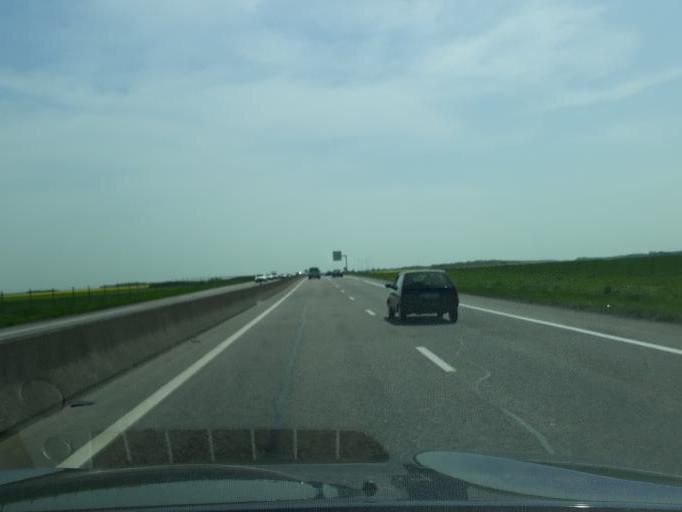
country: FR
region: Ile-de-France
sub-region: Departement des Yvelines
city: Sonchamp
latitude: 48.5855
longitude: 1.8321
